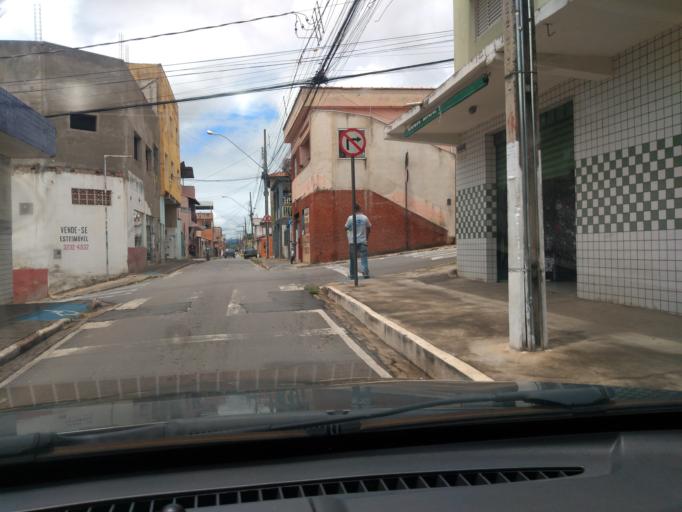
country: BR
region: Minas Gerais
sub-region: Tres Coracoes
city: Tres Coracoes
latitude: -21.6927
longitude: -45.2526
